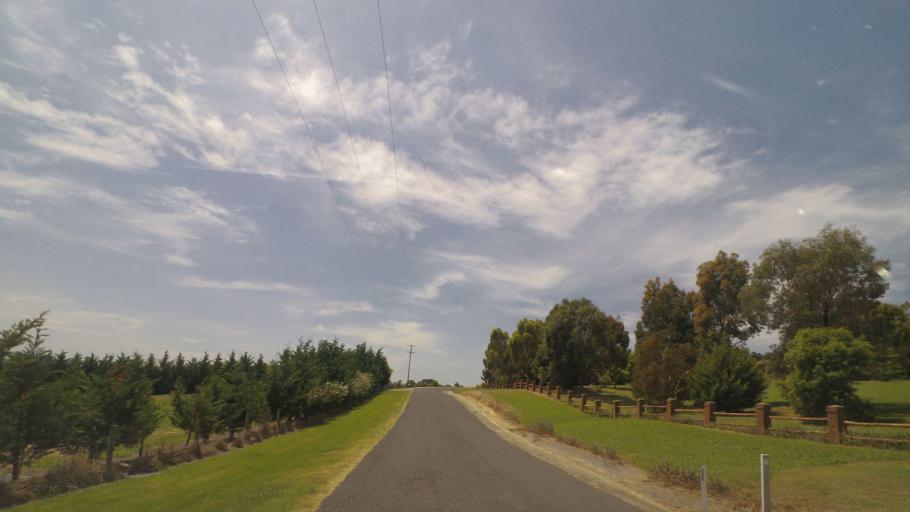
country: AU
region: Victoria
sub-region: Yarra Ranges
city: Chirnside Park
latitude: -37.7529
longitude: 145.3006
